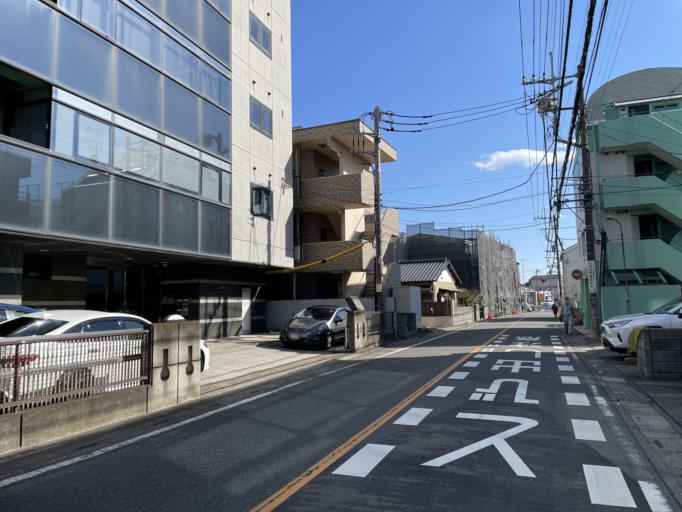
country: JP
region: Saitama
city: Oi
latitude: 35.8568
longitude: 139.5138
